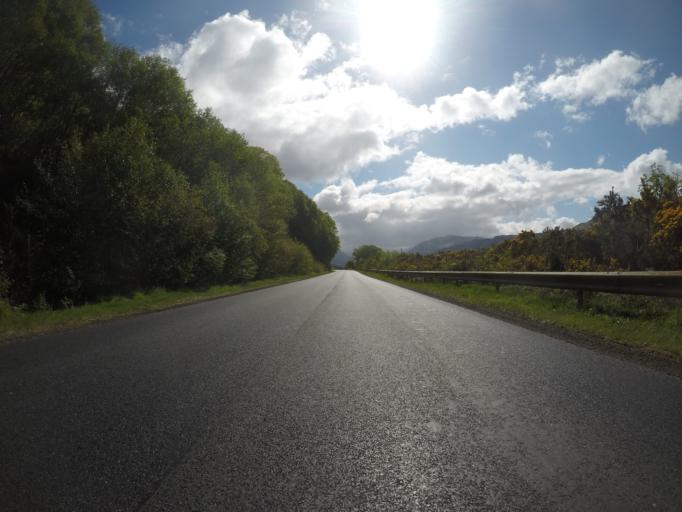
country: GB
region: Scotland
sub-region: Highland
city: Fort William
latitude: 57.2634
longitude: -5.5009
